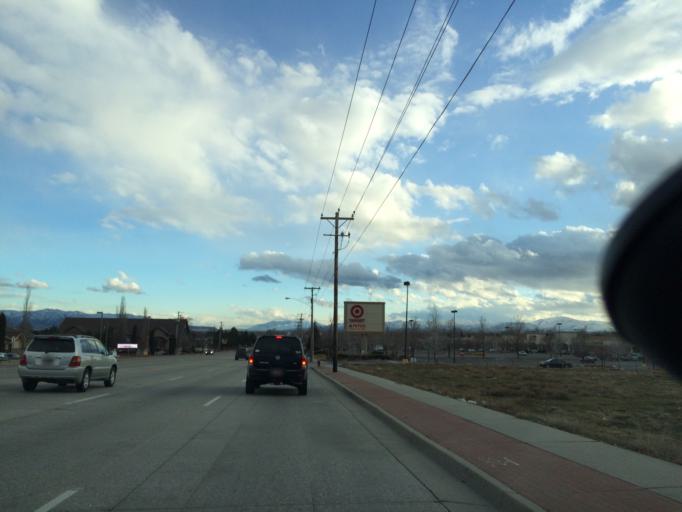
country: US
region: Utah
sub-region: Salt Lake County
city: West Jordan
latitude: 40.6301
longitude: -111.9389
